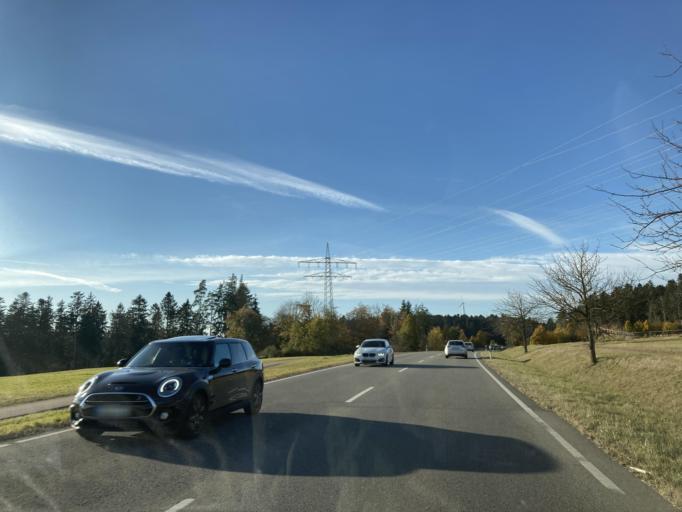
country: DE
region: Baden-Wuerttemberg
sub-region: Karlsruhe Region
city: Schopfloch
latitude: 48.4617
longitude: 8.5419
